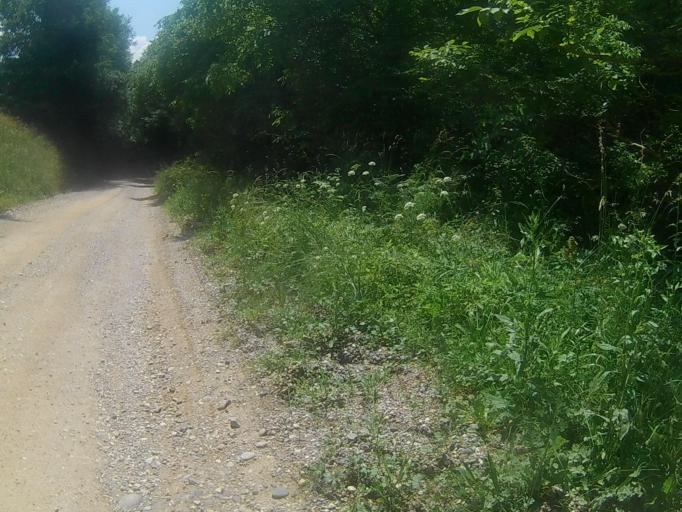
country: SI
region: Ruse
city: Bistrica ob Dravi
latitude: 46.5853
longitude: 15.5380
